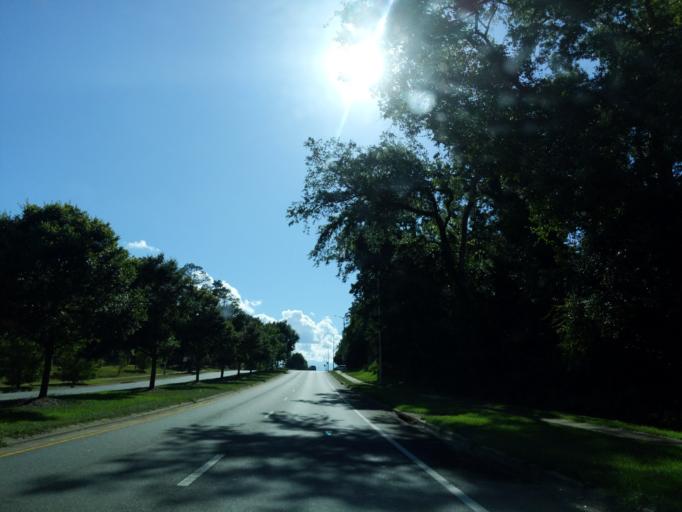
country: US
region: Florida
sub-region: Leon County
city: Tallahassee
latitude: 30.4108
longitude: -84.2423
